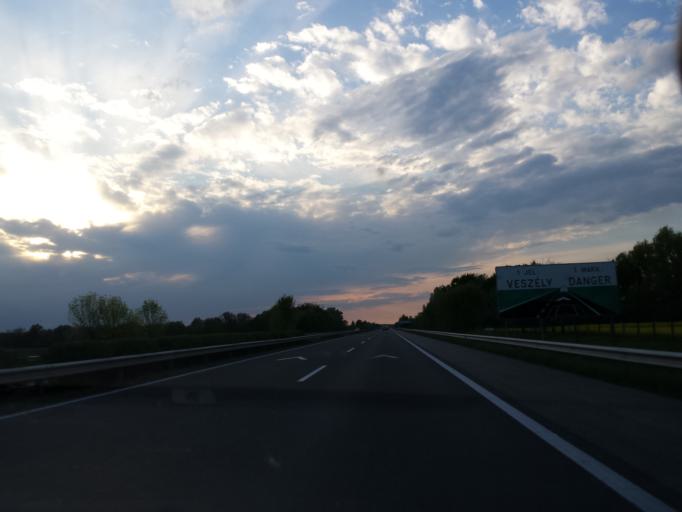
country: HU
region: Gyor-Moson-Sopron
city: Otteveny
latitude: 47.7158
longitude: 17.4716
